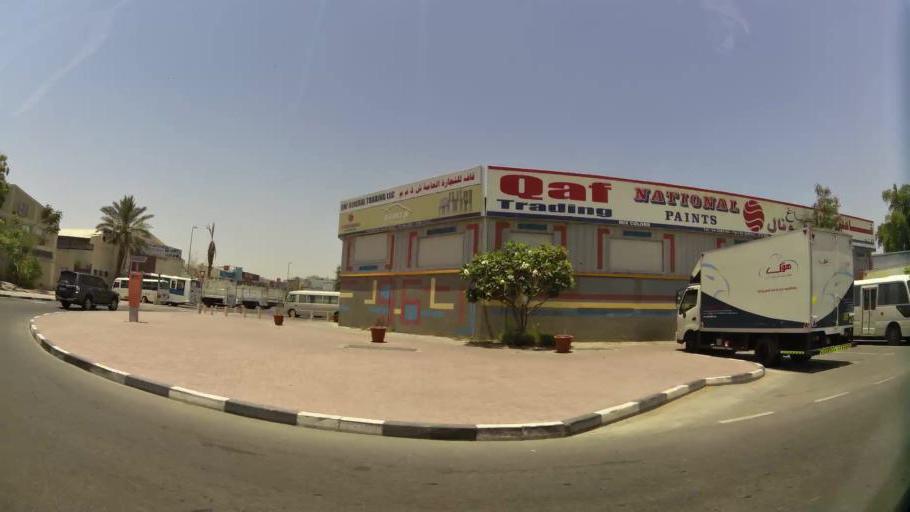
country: AE
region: Ash Shariqah
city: Sharjah
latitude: 25.2690
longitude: 55.3353
